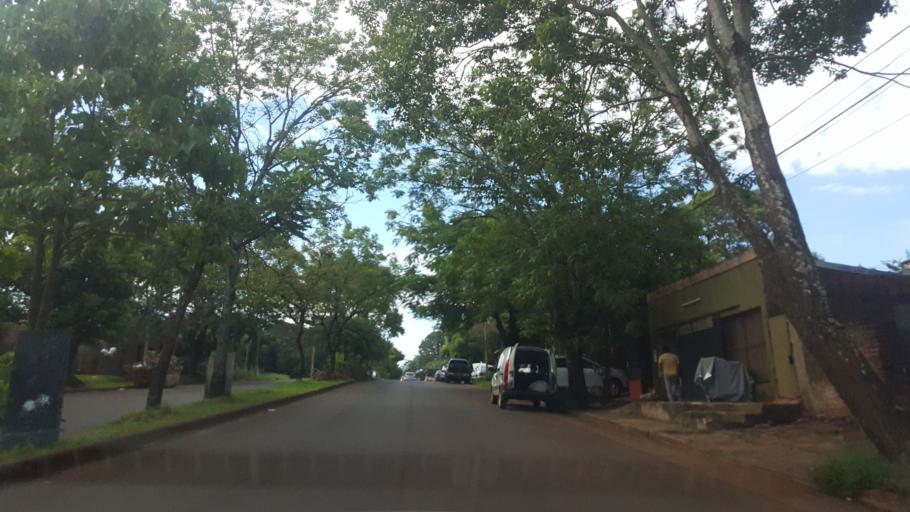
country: AR
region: Misiones
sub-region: Departamento de Capital
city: Posadas
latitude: -27.3692
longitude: -55.9319
